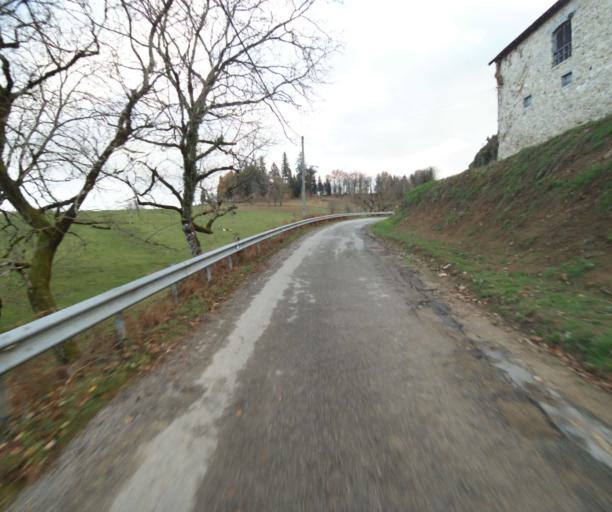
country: FR
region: Limousin
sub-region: Departement de la Correze
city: Laguenne
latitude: 45.2293
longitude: 1.7749
